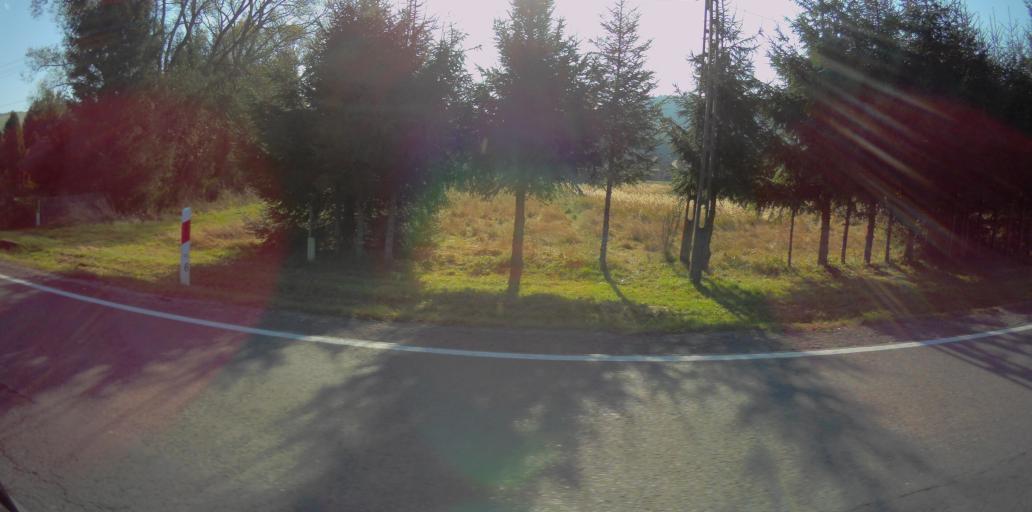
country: PL
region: Subcarpathian Voivodeship
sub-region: Powiat bieszczadzki
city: Ustrzyki Dolne
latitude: 49.4704
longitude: 22.6522
